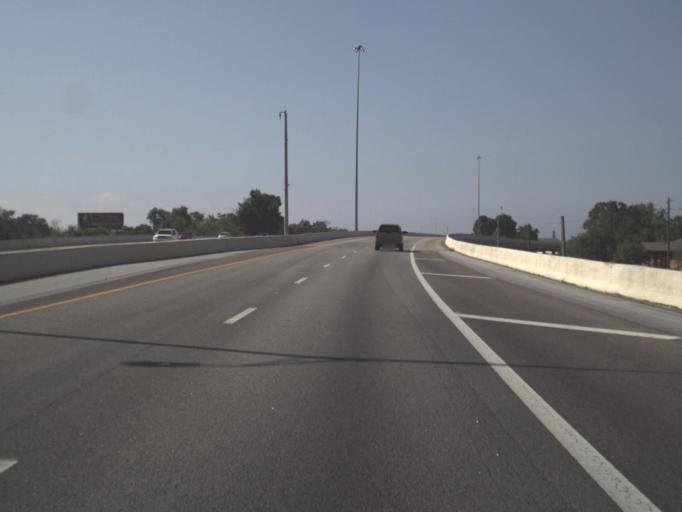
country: US
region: Florida
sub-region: Escambia County
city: Goulding
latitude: 30.4364
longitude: -87.2158
